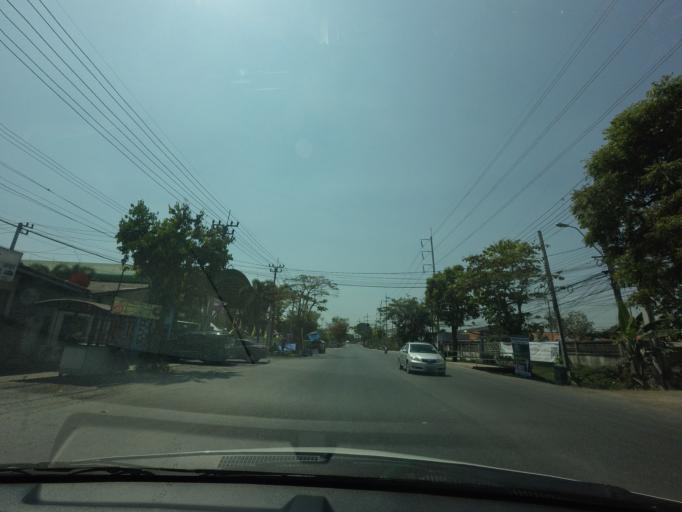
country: TH
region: Bangkok
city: Nong Chok
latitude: 13.8596
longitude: 100.8533
